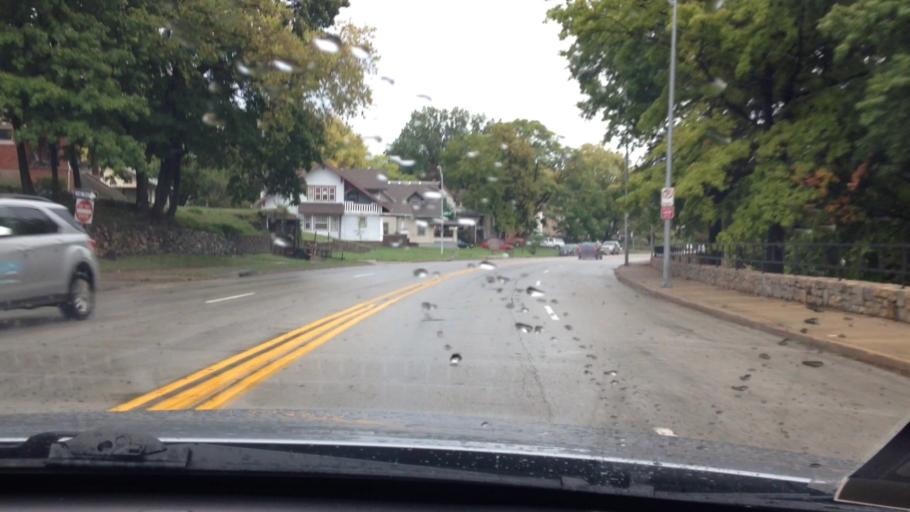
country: US
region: Missouri
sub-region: Jackson County
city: Kansas City
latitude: 39.0744
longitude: -94.5665
